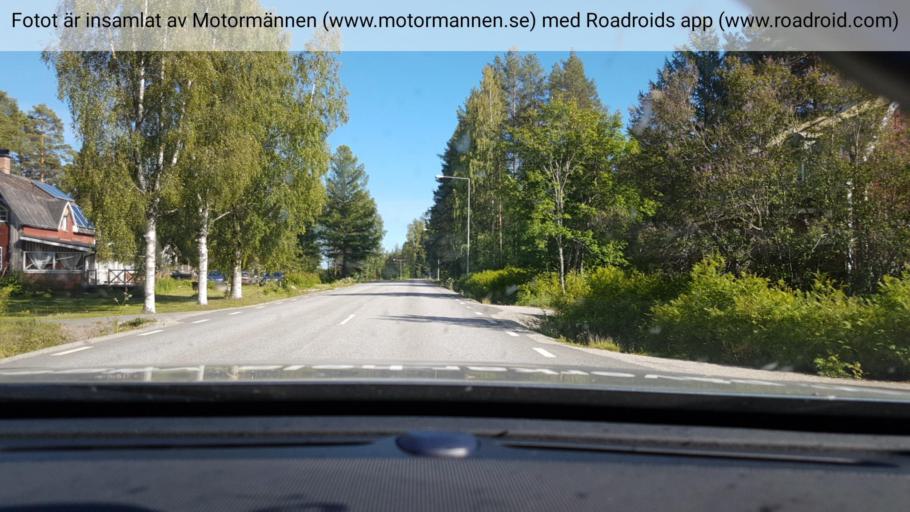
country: SE
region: Vaesterbotten
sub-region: Lycksele Kommun
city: Lycksele
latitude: 64.6365
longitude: 18.5357
